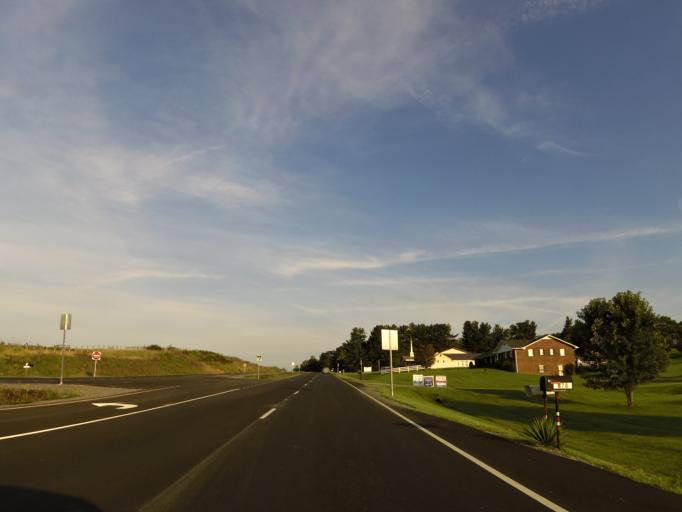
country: US
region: Virginia
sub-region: Washington County
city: Abingdon
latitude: 36.6839
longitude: -81.8839
